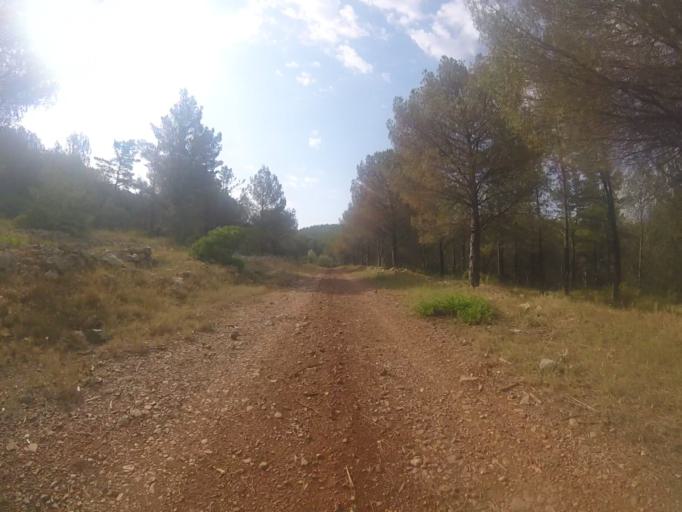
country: ES
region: Valencia
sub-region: Provincia de Castello
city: Cervera del Maestre
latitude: 40.3969
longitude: 0.2070
